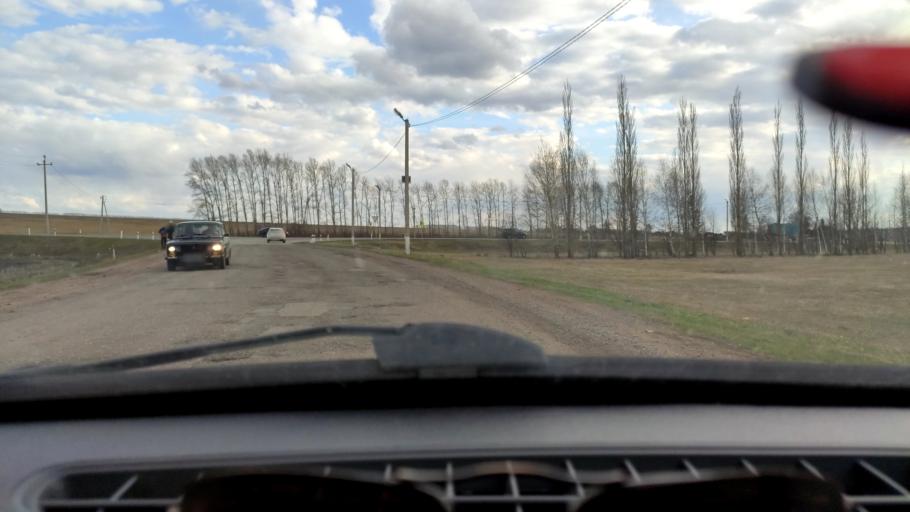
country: RU
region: Bashkortostan
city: Karmaskaly
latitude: 54.3902
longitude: 56.2387
